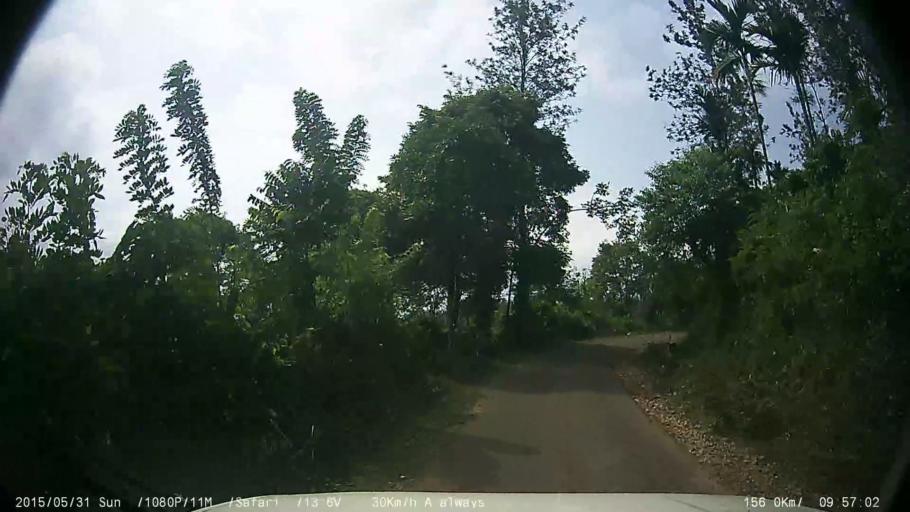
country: IN
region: Kerala
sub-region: Wayanad
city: Kalpetta
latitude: 11.5957
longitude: 76.0580
